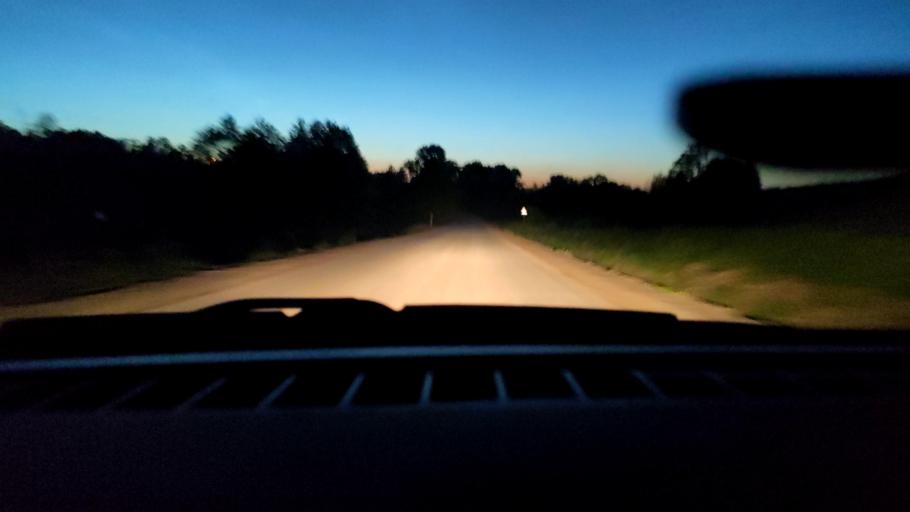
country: RU
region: Perm
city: Kultayevo
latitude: 57.8638
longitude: 55.9842
